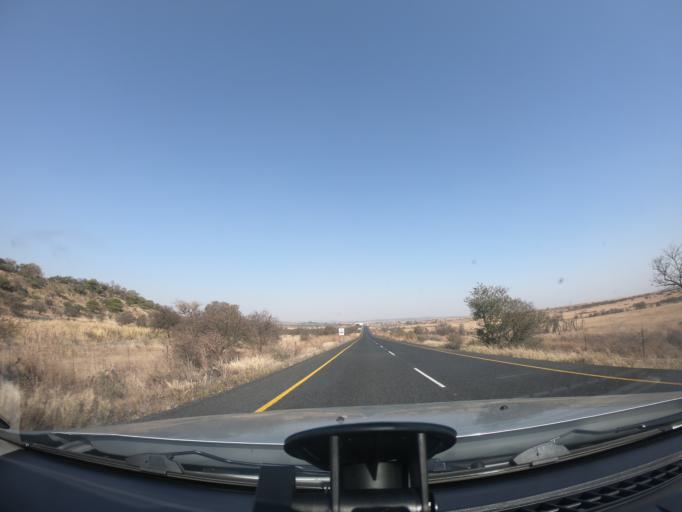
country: ZA
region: KwaZulu-Natal
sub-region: uThukela District Municipality
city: Ladysmith
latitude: -28.7221
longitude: 29.8130
